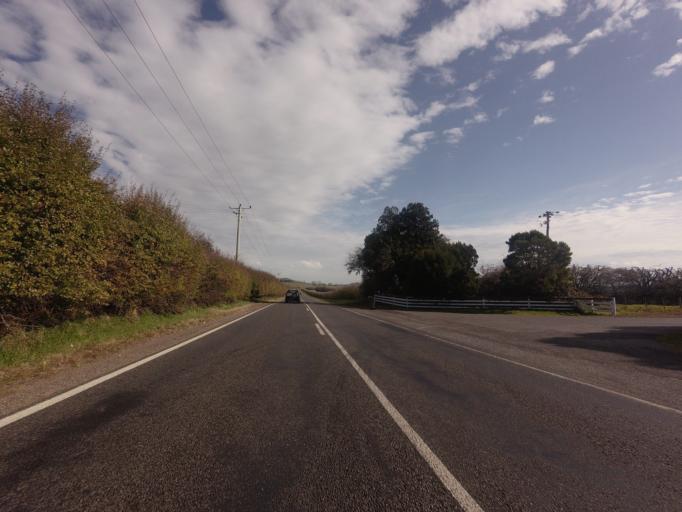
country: AU
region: Tasmania
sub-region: Meander Valley
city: Westbury
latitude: -41.5240
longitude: 146.7723
